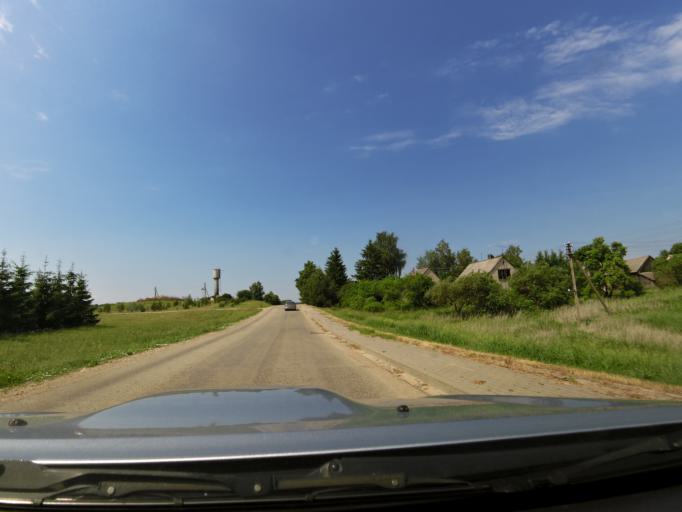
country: LT
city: Vilkaviskis
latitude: 54.5017
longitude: 23.0222
